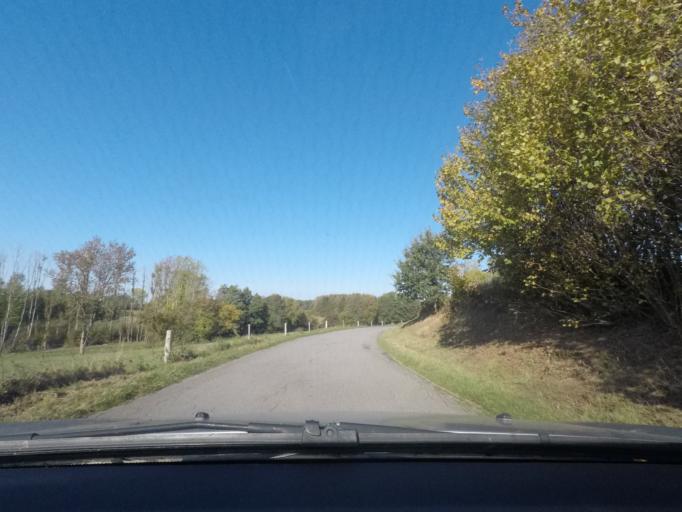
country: BE
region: Wallonia
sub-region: Province du Luxembourg
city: Etalle
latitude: 49.6808
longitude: 5.5937
